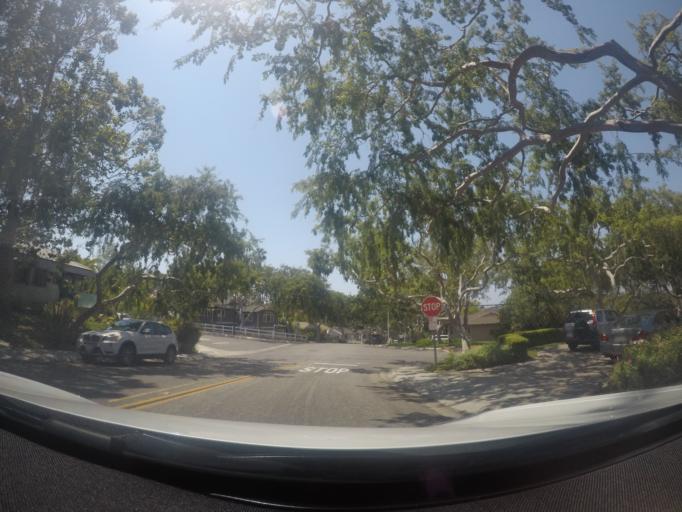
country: US
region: California
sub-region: Los Angeles County
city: Palos Verdes Estates
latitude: 33.8163
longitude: -118.3735
